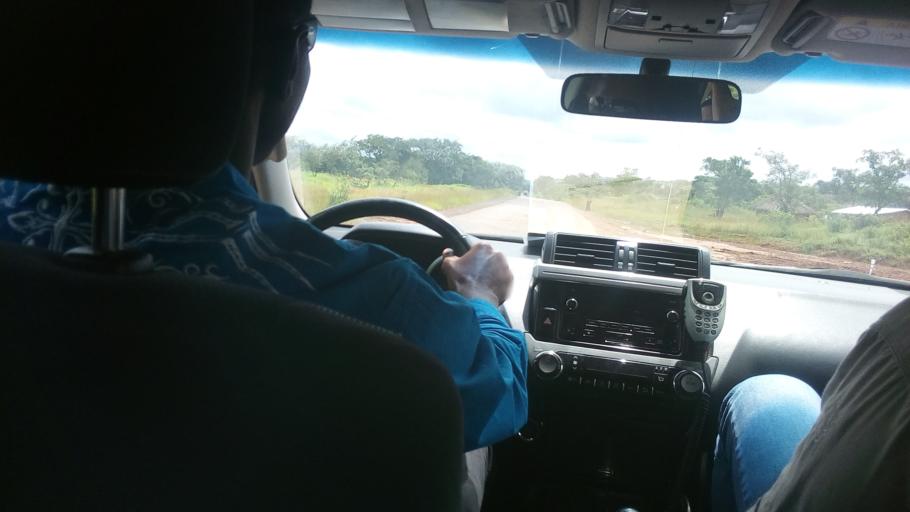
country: GN
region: Boke
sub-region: Boke Prefecture
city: Boke
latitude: 11.0230
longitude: -14.0663
